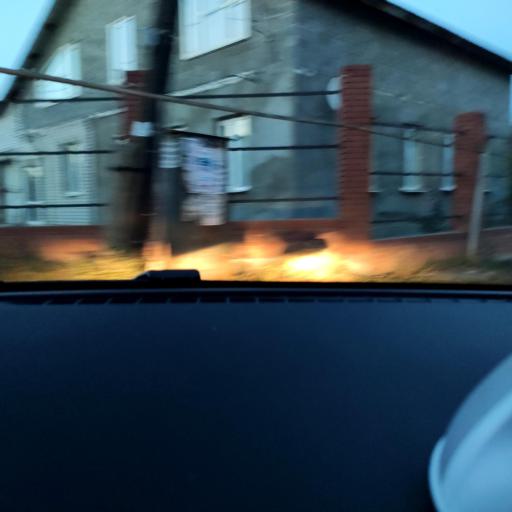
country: RU
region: Samara
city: Petra-Dubrava
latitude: 53.2996
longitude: 50.3033
